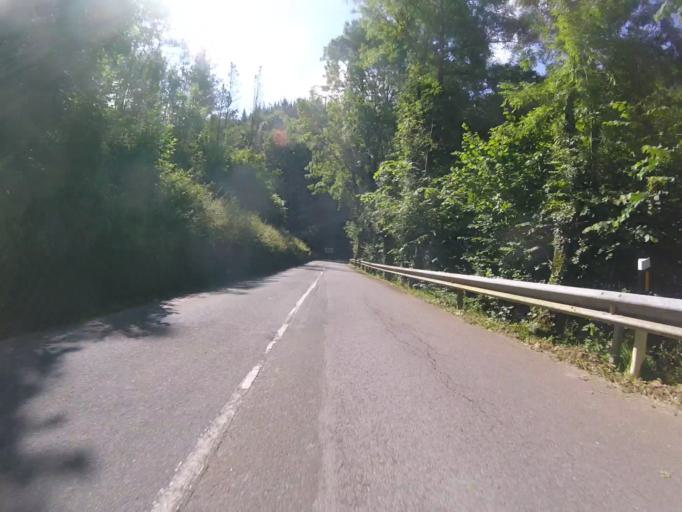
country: ES
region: Basque Country
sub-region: Provincia de Guipuzcoa
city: Beizama
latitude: 43.0975
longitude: -2.2383
